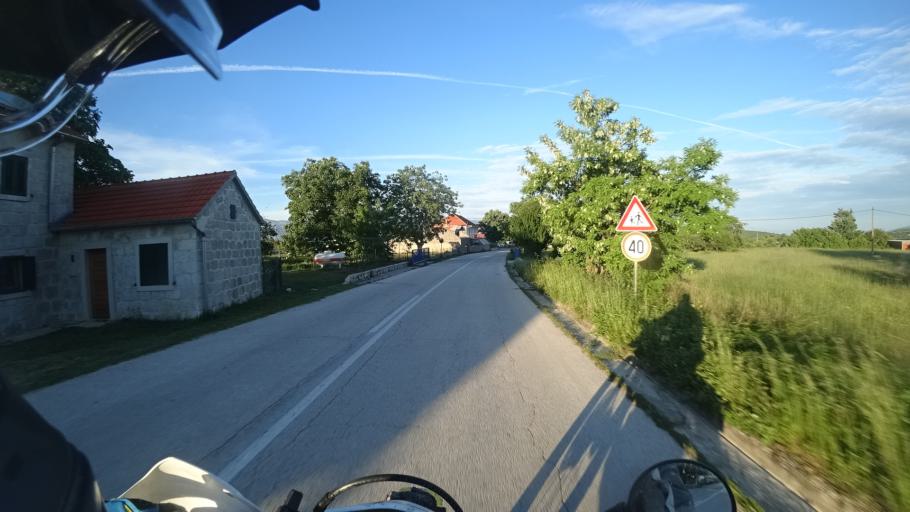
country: HR
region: Sibensko-Kniniska
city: Drnis
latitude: 43.8956
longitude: 16.3819
